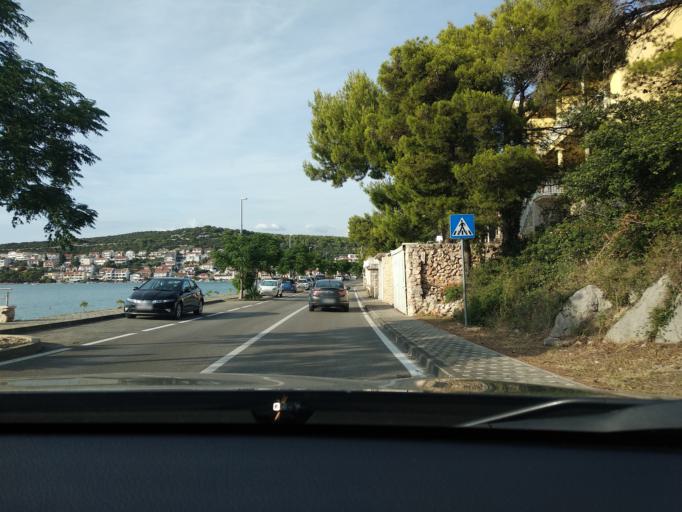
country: HR
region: Sibensko-Kniniska
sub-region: Grad Sibenik
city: Tisno
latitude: 43.7969
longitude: 15.6341
